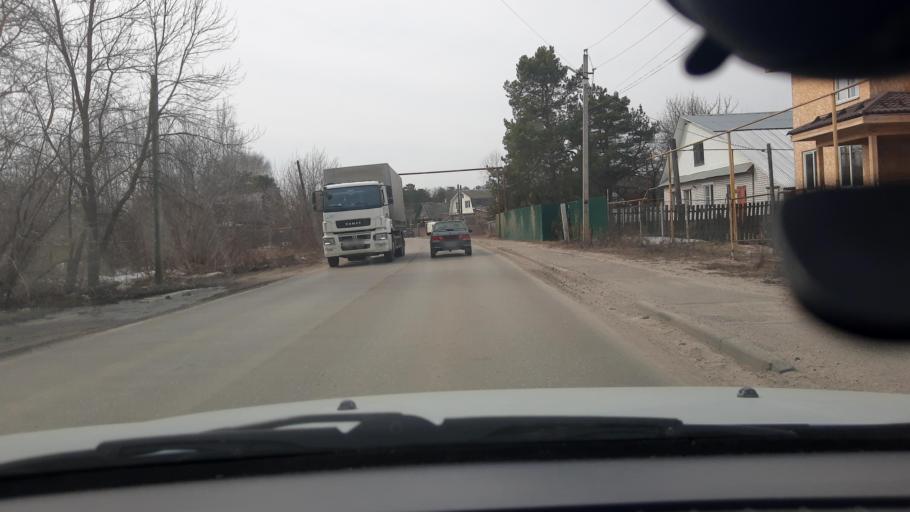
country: RU
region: Nizjnij Novgorod
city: Novaya Balakhna
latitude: 56.4834
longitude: 43.5719
